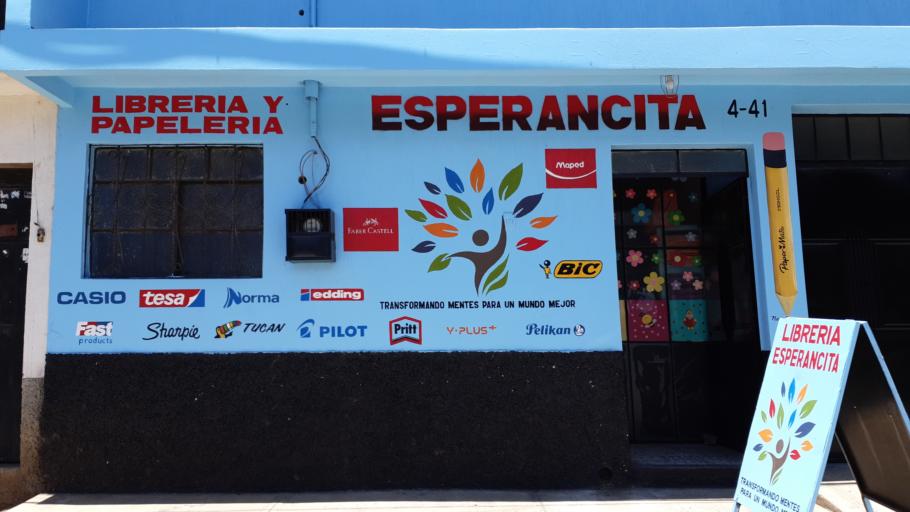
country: GT
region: Chimaltenango
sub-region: Municipio de Chimaltenango
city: Chimaltenango
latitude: 14.6619
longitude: -90.8376
